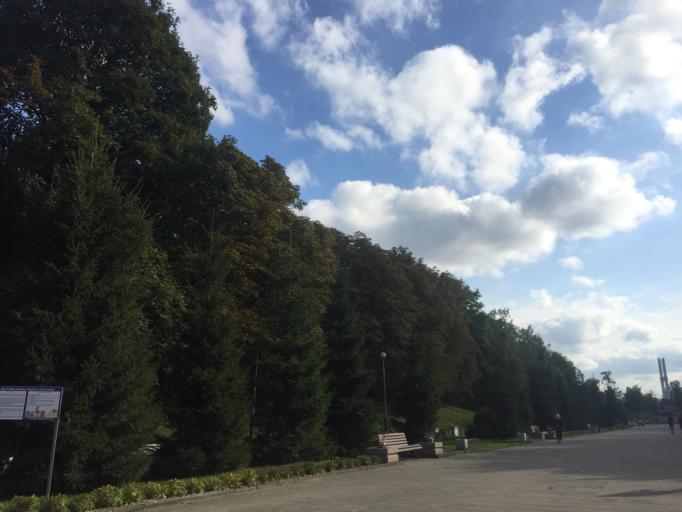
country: RU
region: Kaliningrad
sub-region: Gorod Kaliningrad
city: Kaliningrad
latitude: 54.6949
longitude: 20.5097
